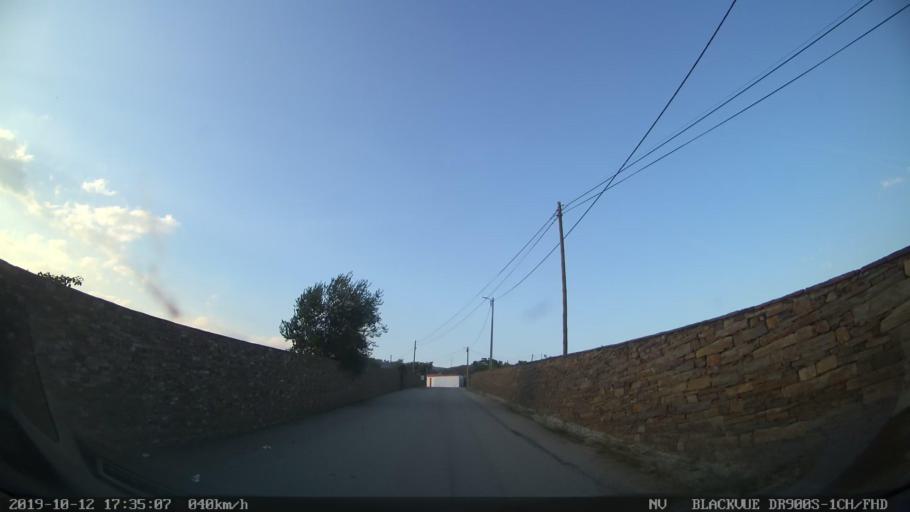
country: PT
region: Vila Real
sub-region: Peso da Regua
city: Godim
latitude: 41.1526
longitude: -7.8155
